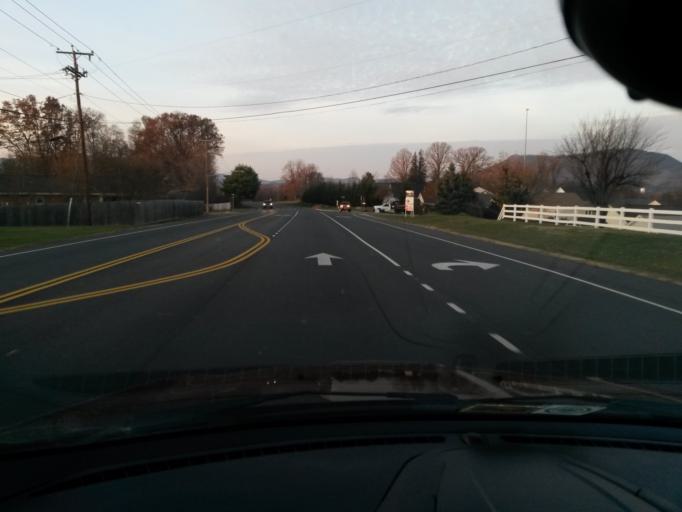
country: US
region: Virginia
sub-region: Roanoke County
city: Hollins
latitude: 37.3376
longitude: -79.9416
